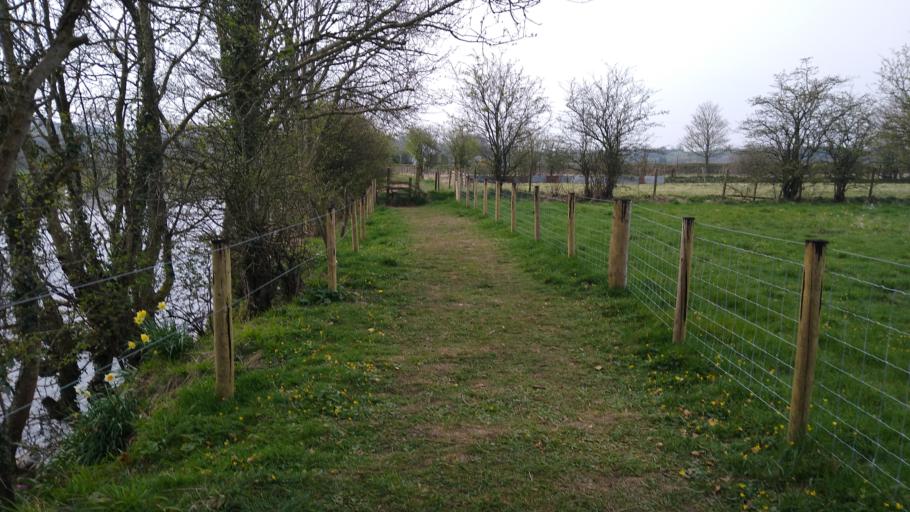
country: GB
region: England
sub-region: Cumbria
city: Dearham
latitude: 54.6655
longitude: -3.4348
